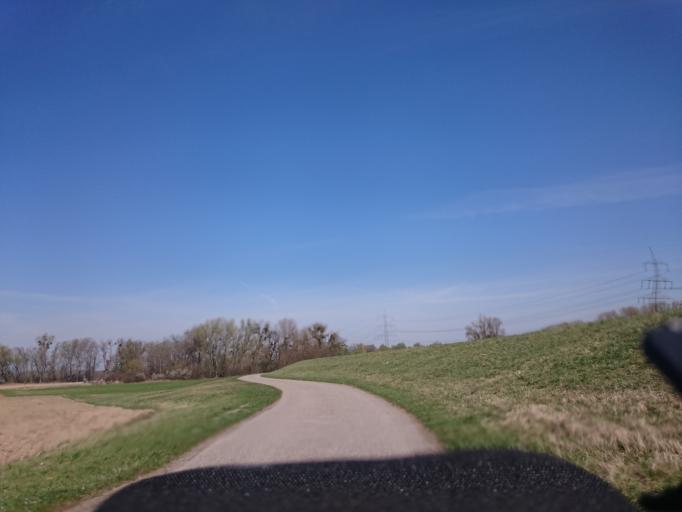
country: DE
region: Rheinland-Pfalz
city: Neuburg
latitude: 49.0139
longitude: 8.2720
